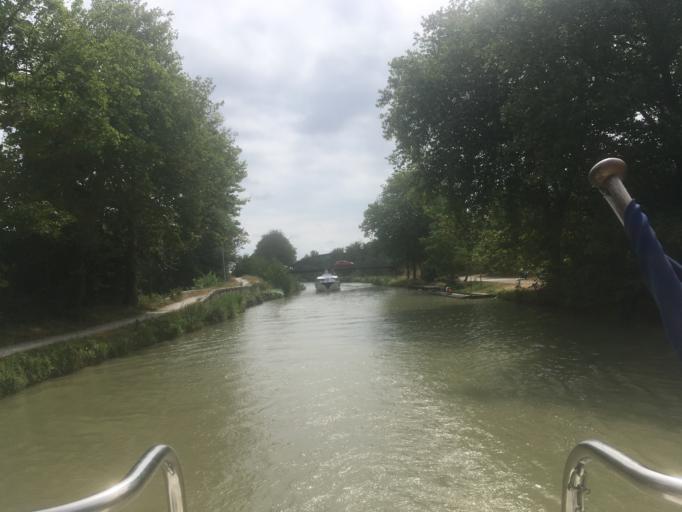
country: FR
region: Languedoc-Roussillon
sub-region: Departement de l'Aude
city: Villepinte
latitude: 43.2760
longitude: 2.0772
